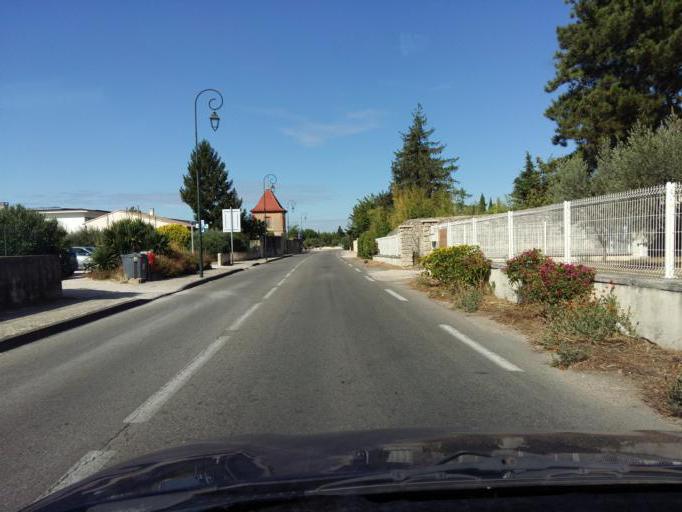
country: FR
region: Provence-Alpes-Cote d'Azur
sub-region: Departement du Vaucluse
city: Mazan
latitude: 44.0579
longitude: 5.1230
